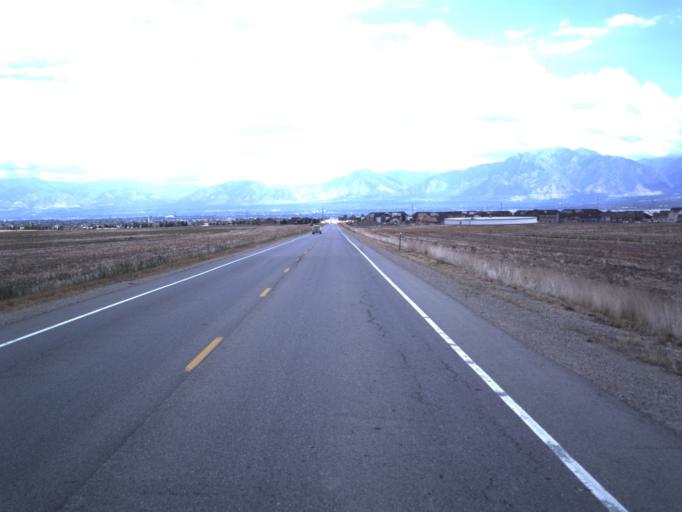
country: US
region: Utah
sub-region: Salt Lake County
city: Oquirrh
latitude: 40.5790
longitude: -112.0552
